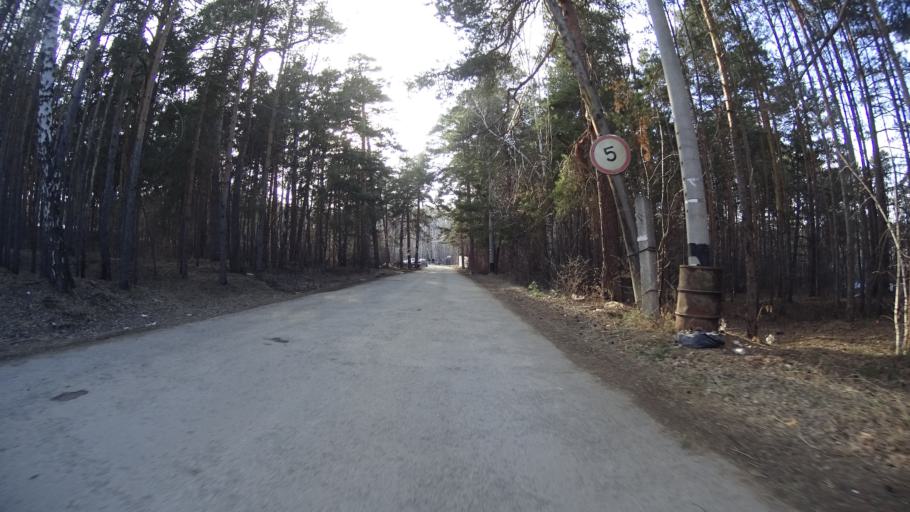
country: RU
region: Chelyabinsk
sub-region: Gorod Chelyabinsk
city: Chelyabinsk
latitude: 55.1286
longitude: 61.3577
